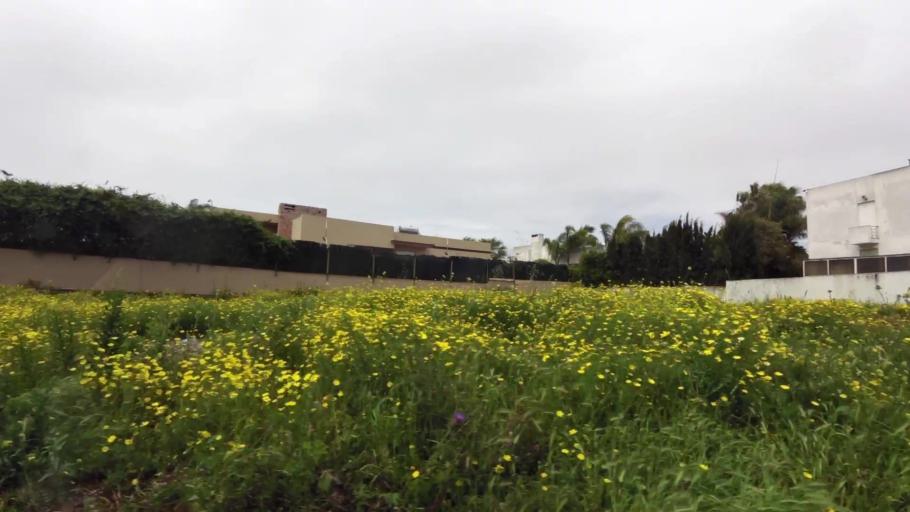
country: MA
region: Grand Casablanca
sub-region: Casablanca
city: Casablanca
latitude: 33.5326
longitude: -7.6420
